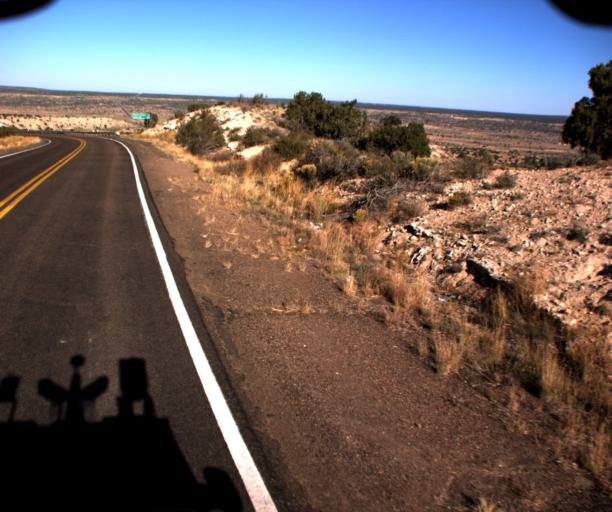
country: US
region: Arizona
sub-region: Navajo County
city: First Mesa
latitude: 35.7337
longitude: -110.1091
